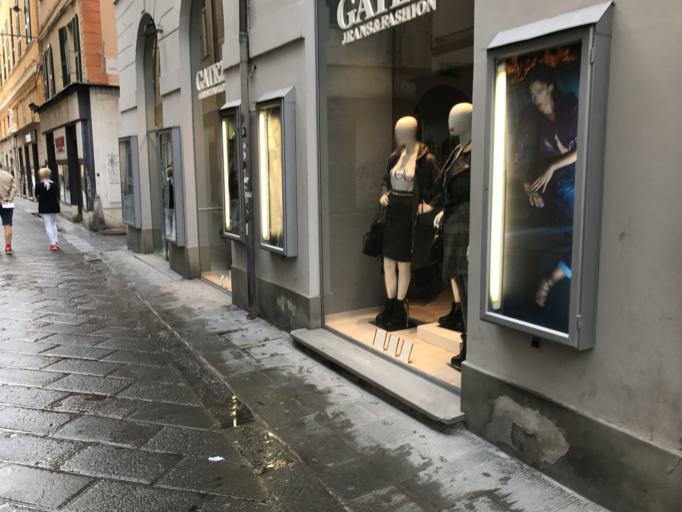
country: IT
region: Liguria
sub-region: Provincia di La Spezia
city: La Spezia
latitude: 44.1048
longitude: 9.8210
